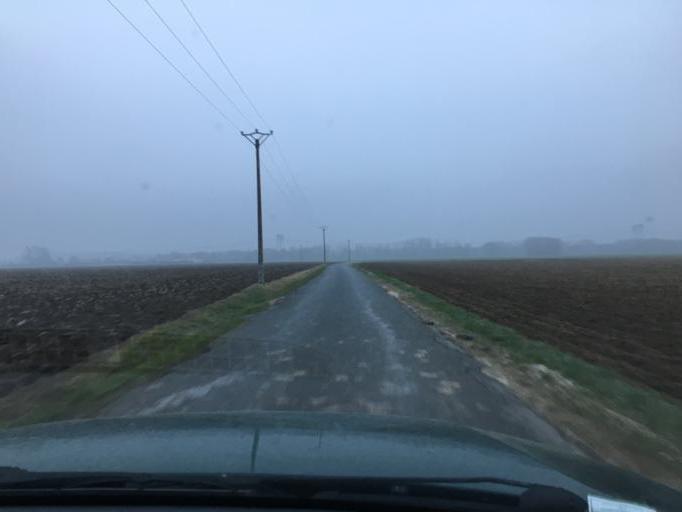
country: FR
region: Centre
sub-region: Departement du Loiret
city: Beaugency
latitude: 47.7687
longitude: 1.6535
